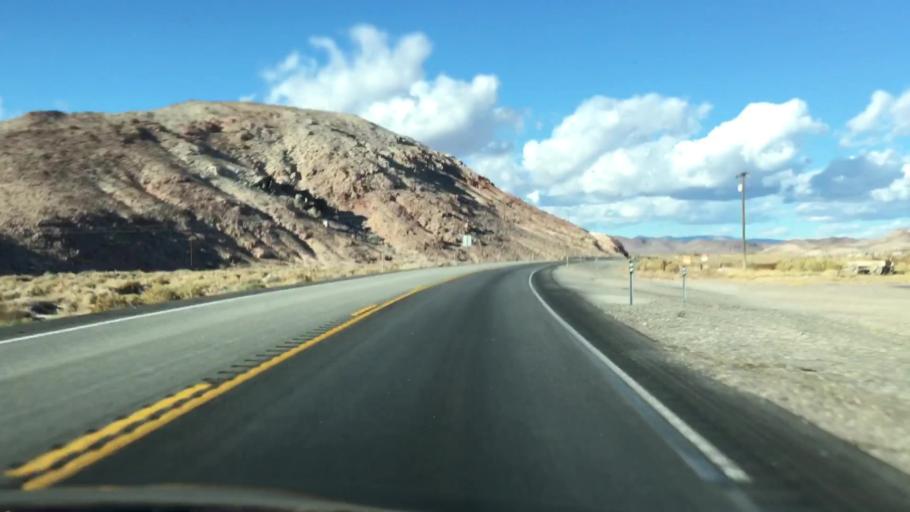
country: US
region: Nevada
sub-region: Nye County
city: Beatty
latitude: 36.9738
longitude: -116.7235
